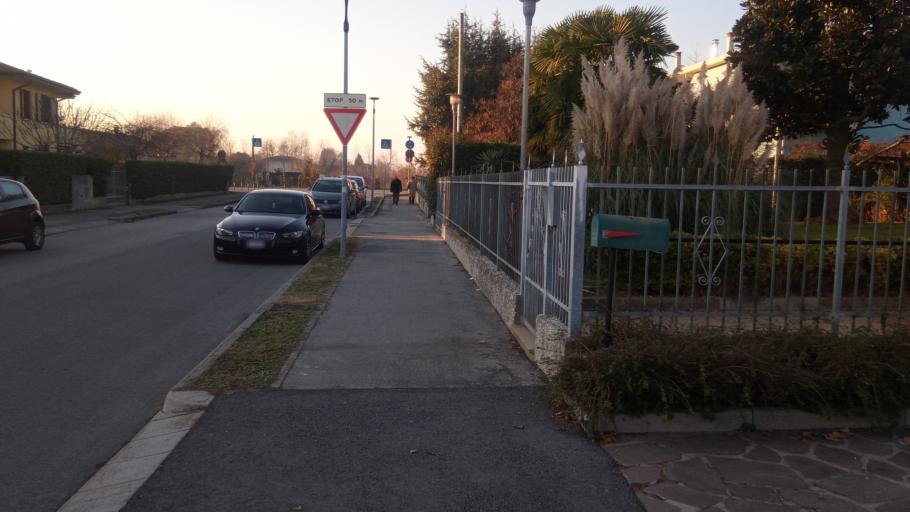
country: IT
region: Veneto
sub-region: Provincia di Padova
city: Rubano
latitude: 45.4318
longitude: 11.7896
